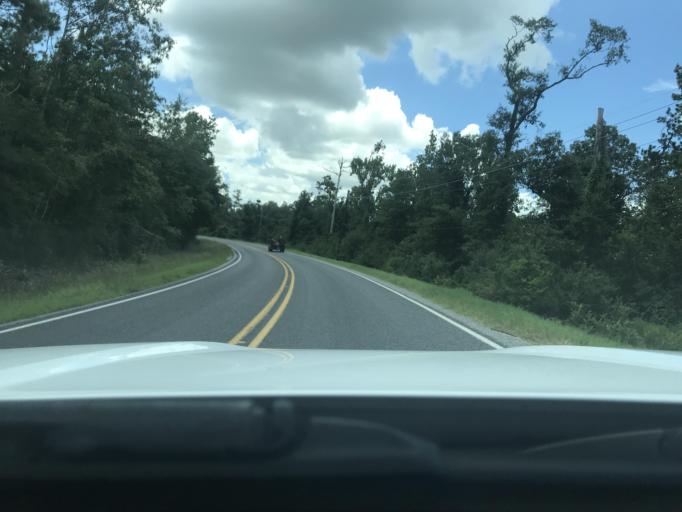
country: US
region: Louisiana
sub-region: Calcasieu Parish
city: Moss Bluff
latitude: 30.2851
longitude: -93.1673
